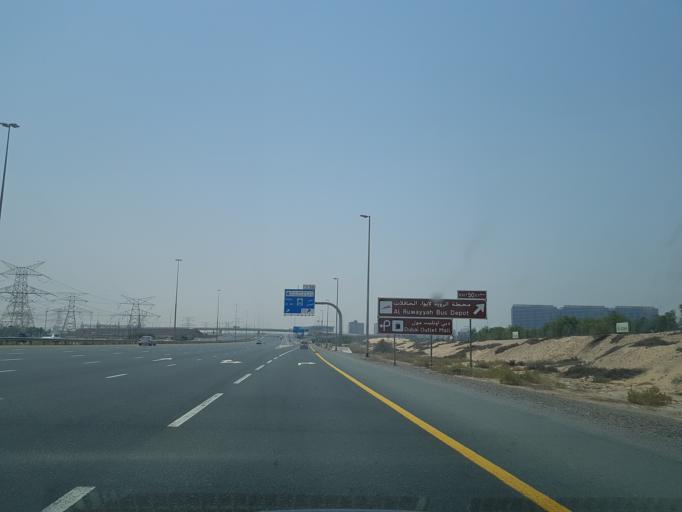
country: AE
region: Dubai
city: Dubai
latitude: 25.0928
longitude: 55.3996
